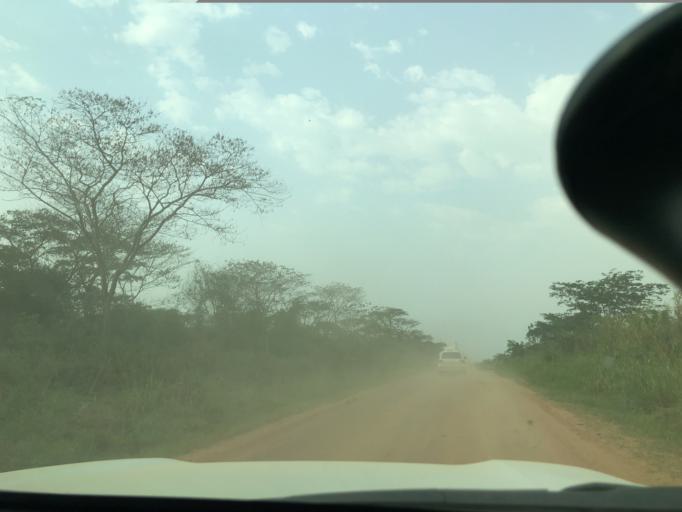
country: UG
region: Western Region
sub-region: Kasese District
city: Margherita
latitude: 0.2172
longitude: 29.6789
